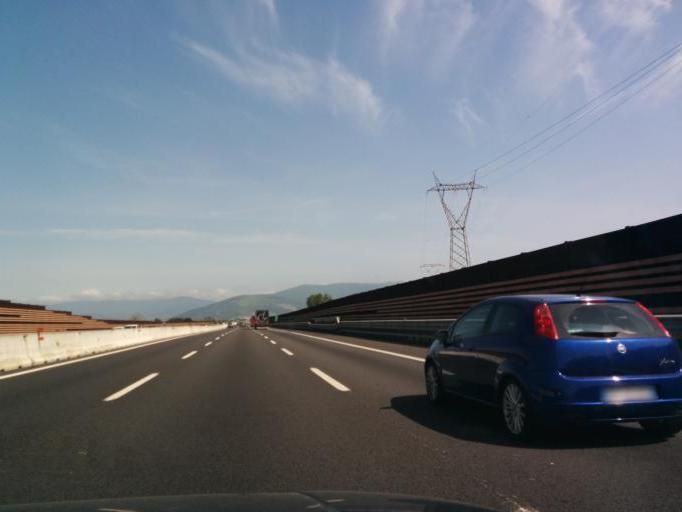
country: IT
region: Tuscany
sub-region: Province of Florence
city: San Donnino
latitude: 43.7954
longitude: 11.1565
